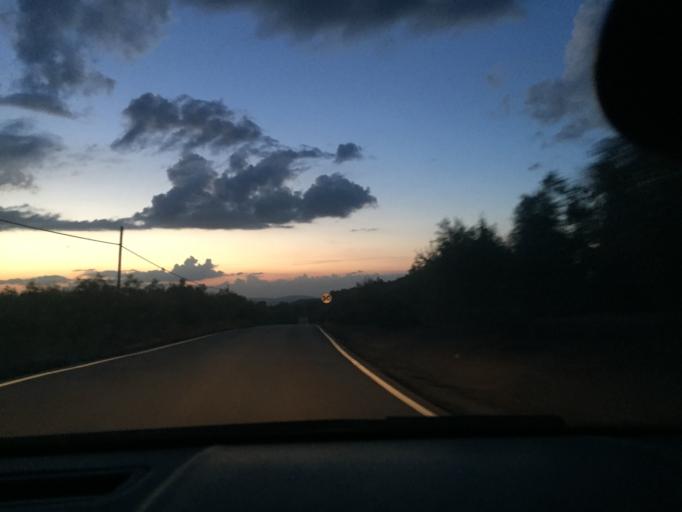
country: ES
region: Andalusia
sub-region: Provincia de Jaen
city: Mancha Real
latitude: 37.7987
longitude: -3.6534
